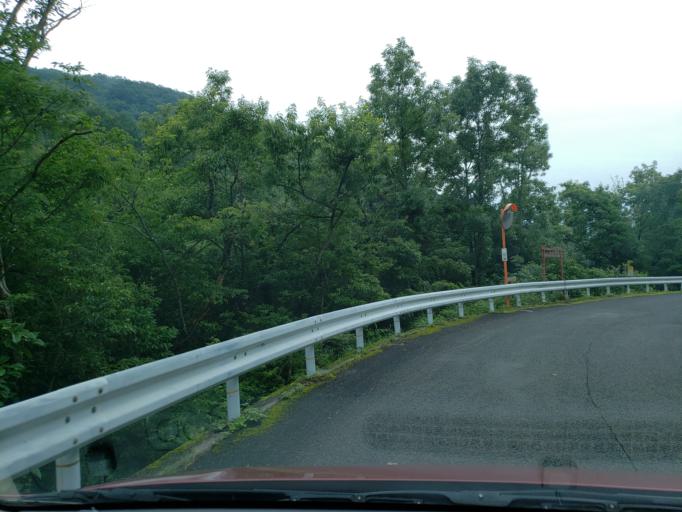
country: JP
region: Tokushima
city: Kamojimacho-jogejima
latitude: 34.1126
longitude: 134.3003
